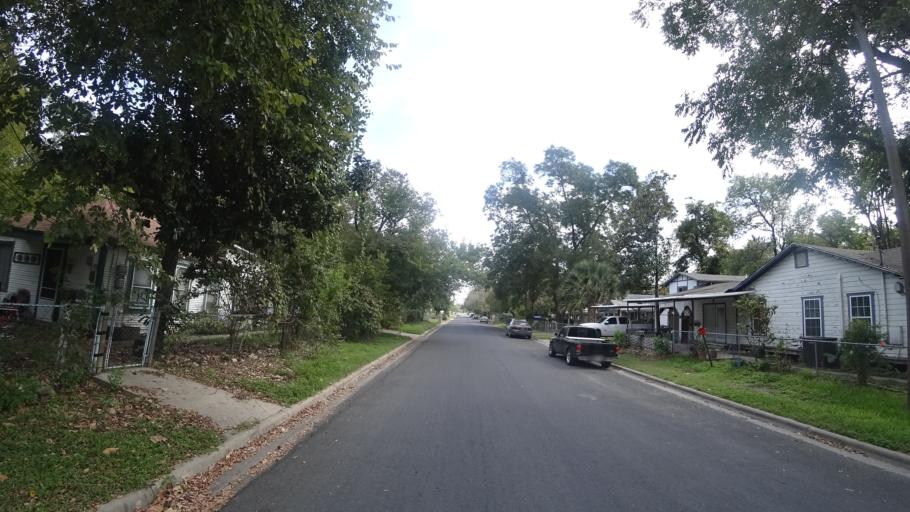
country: US
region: Texas
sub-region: Travis County
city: Austin
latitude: 30.2662
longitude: -97.6982
